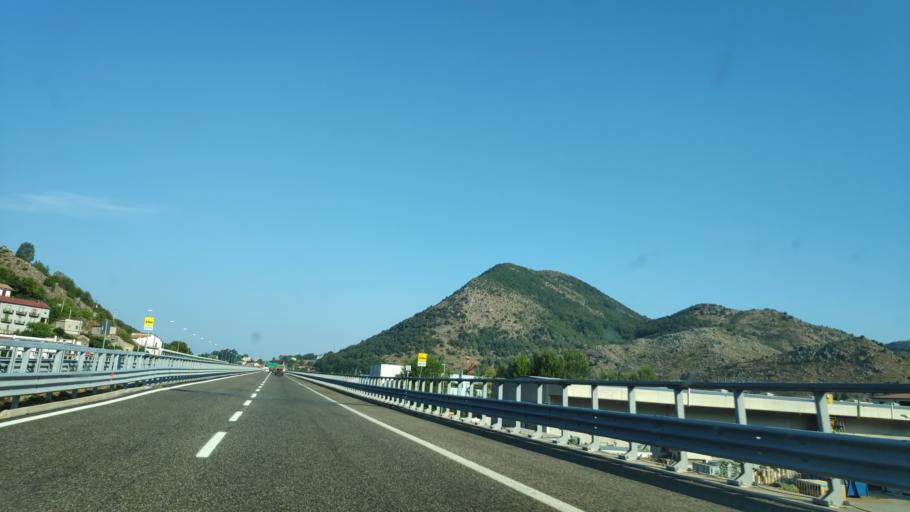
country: IT
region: Basilicate
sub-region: Provincia di Potenza
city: Lauria
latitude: 40.0138
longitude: 15.8976
